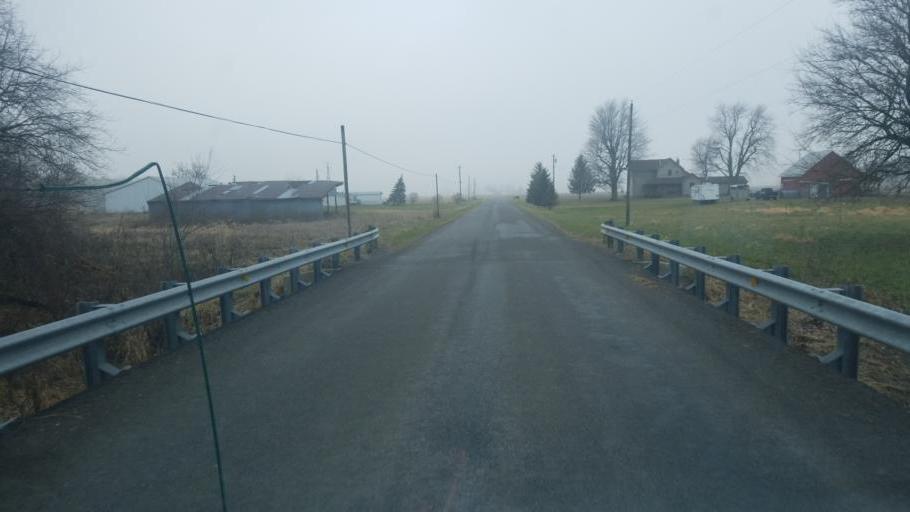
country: US
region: Ohio
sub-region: Hardin County
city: Kenton
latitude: 40.5049
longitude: -83.5204
